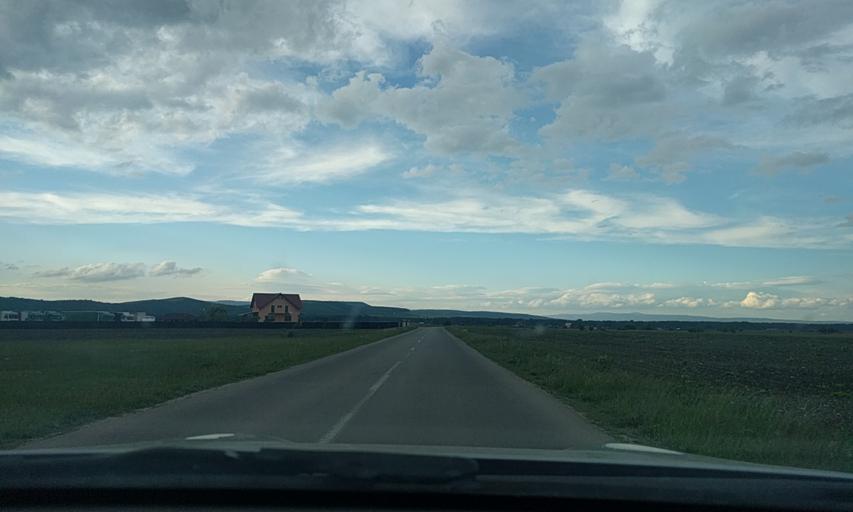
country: RO
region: Brasov
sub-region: Comuna Harman
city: Harman
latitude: 45.7266
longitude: 25.6989
